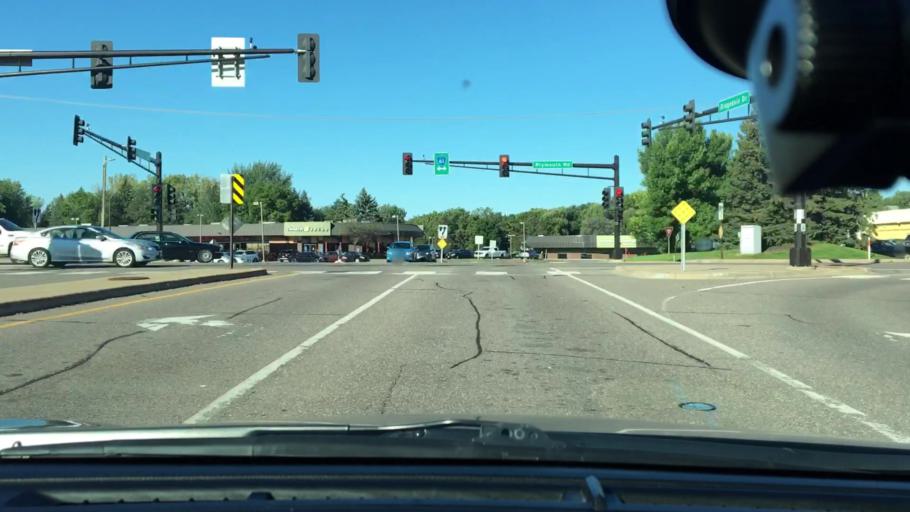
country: US
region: Minnesota
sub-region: Hennepin County
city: Minnetonka Mills
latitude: 44.9658
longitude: -93.4420
